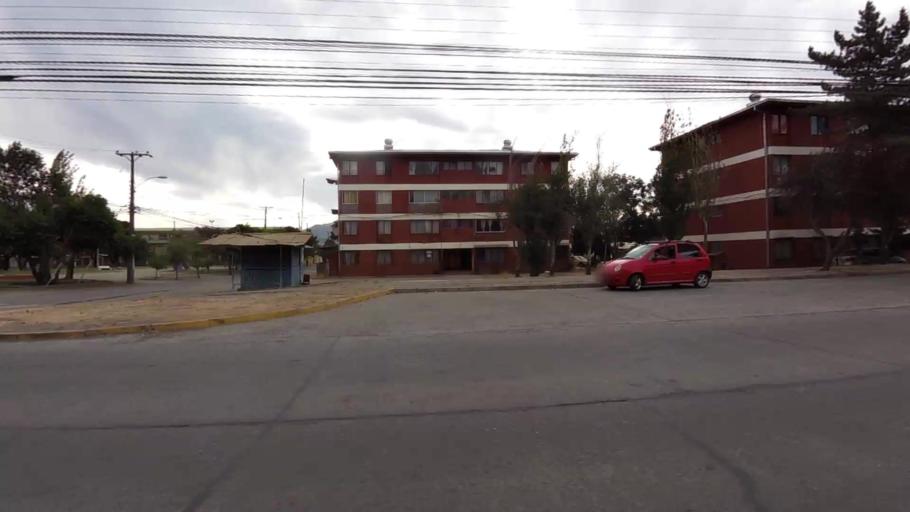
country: CL
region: O'Higgins
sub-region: Provincia de Cachapoal
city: Rancagua
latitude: -34.1523
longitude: -70.7430
